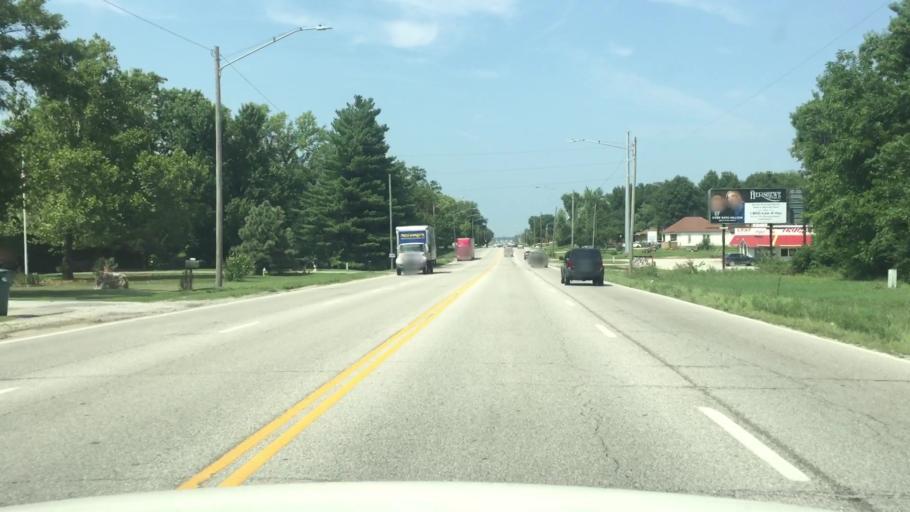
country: US
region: Kansas
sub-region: Crawford County
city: Frontenac
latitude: 37.4472
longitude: -94.7051
